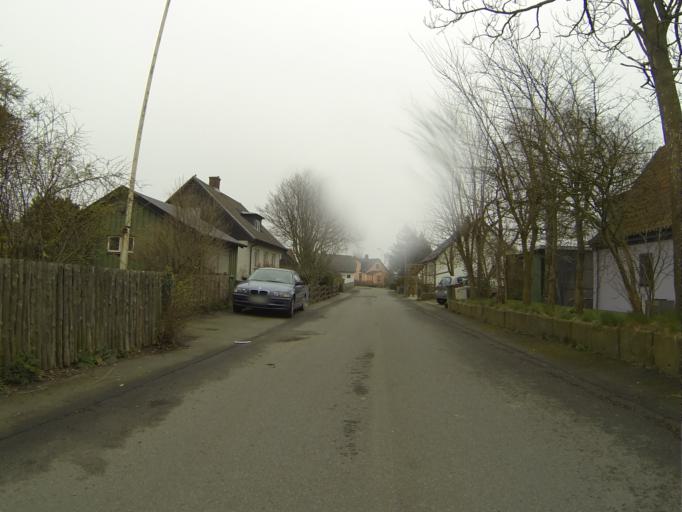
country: SE
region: Skane
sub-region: Simrishamns Kommun
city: Kivik
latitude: 55.5476
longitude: 14.1817
